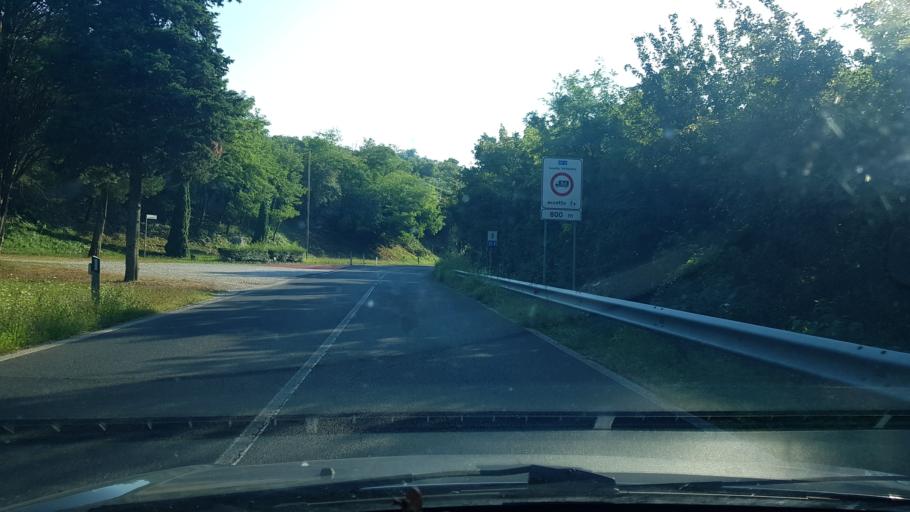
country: IT
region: Friuli Venezia Giulia
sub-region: Provincia di Gorizia
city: Savogna d'Isonzo
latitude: 45.8977
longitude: 13.5498
